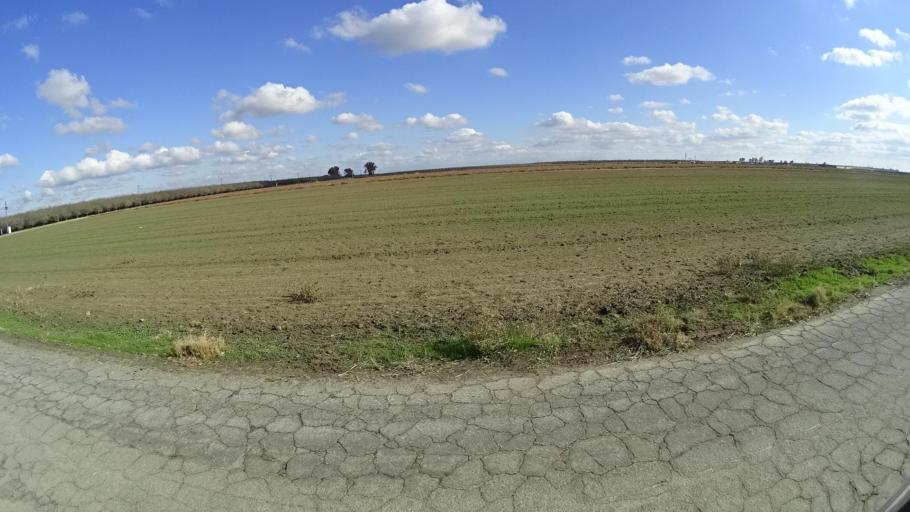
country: US
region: California
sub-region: Kern County
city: Delano
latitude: 35.7455
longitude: -119.3478
